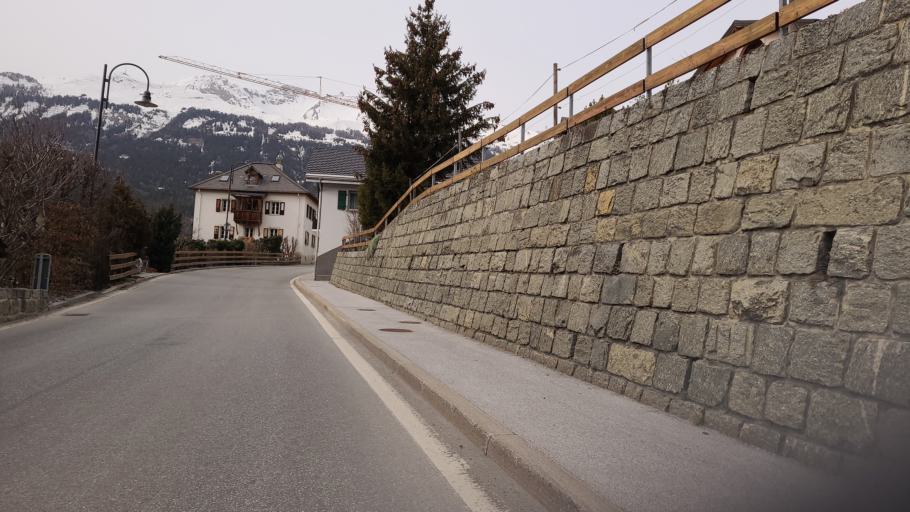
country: CH
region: Valais
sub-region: Sierre District
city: Lens
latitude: 46.2892
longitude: 7.4392
